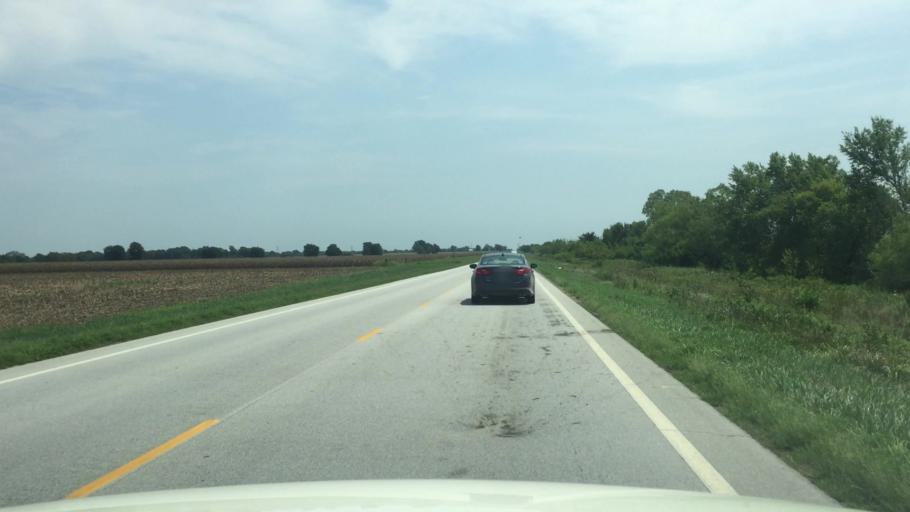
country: US
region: Kansas
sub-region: Cherokee County
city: Columbus
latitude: 37.1792
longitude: -94.9338
